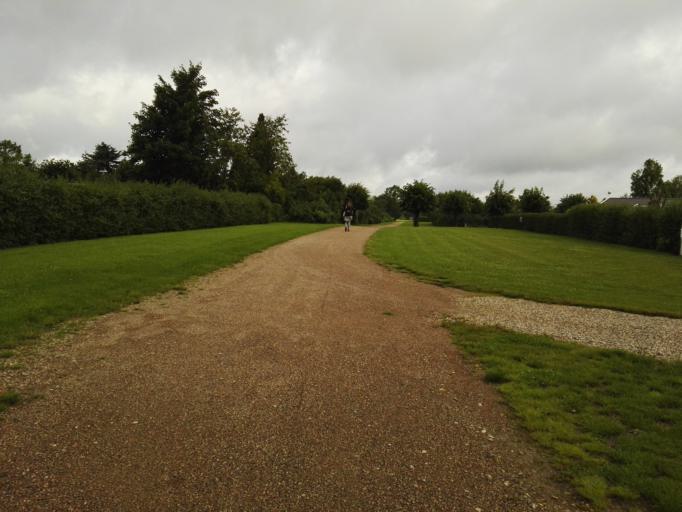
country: DK
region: Capital Region
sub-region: Ballerup Kommune
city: Ballerup
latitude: 55.7127
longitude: 12.3467
